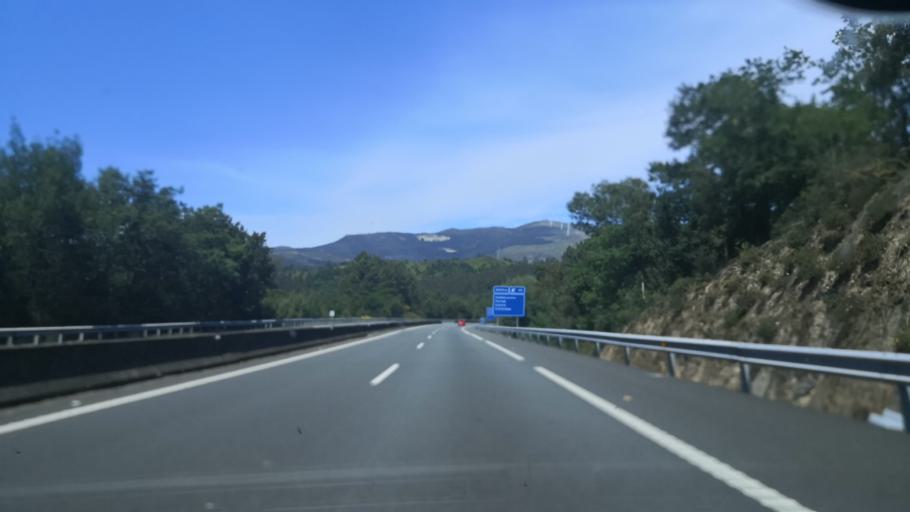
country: ES
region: Galicia
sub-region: Provincia de Pontevedra
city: Portas
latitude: 42.5800
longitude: -8.6740
